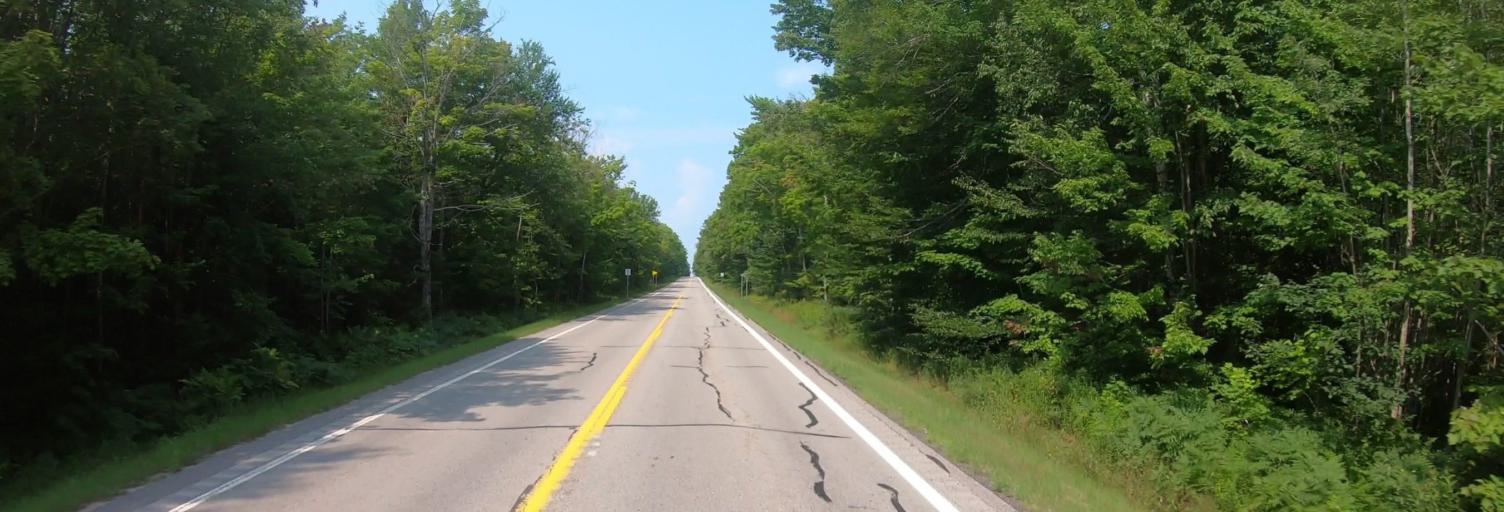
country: US
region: Michigan
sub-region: Luce County
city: Newberry
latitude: 46.5639
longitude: -85.3300
